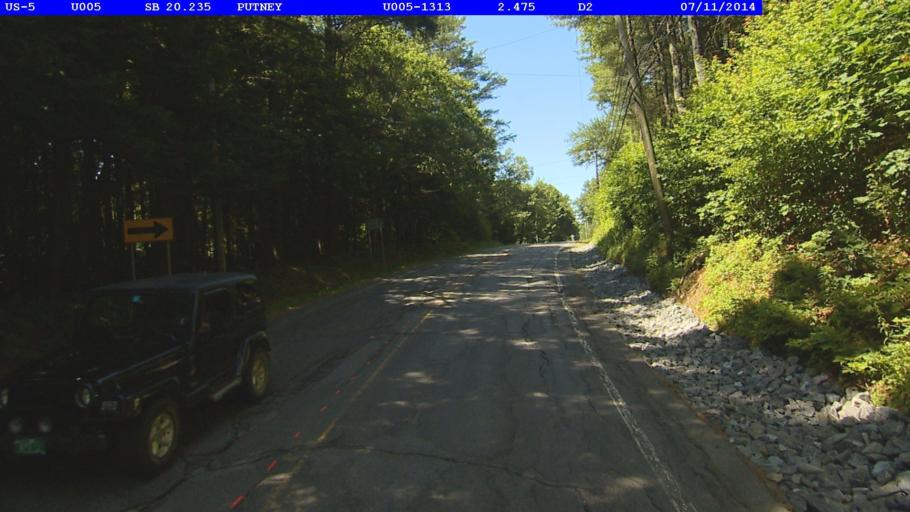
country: US
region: New Hampshire
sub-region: Cheshire County
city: Westmoreland
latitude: 42.9930
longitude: -72.4975
